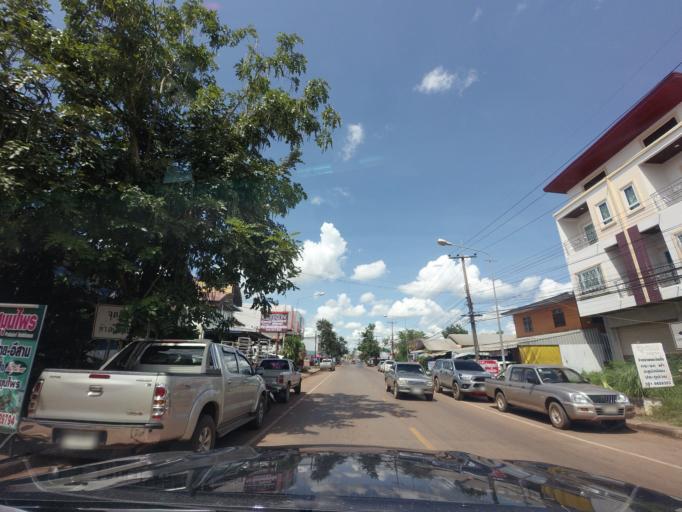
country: TH
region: Changwat Udon Thani
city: Ban Dung
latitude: 17.6942
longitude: 103.2582
